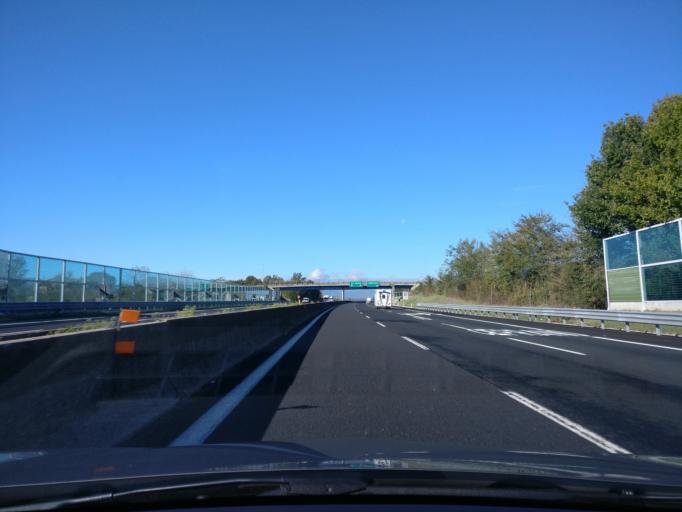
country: IT
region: Latium
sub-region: Provincia di Frosinone
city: Ceprano
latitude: 41.5431
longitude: 13.4977
